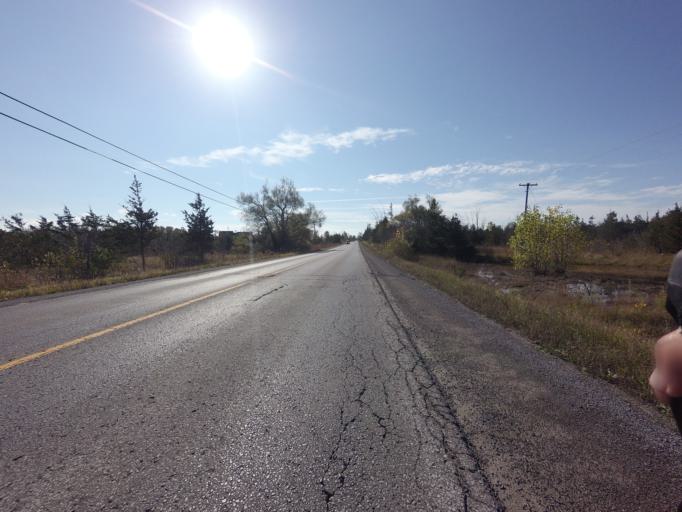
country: CA
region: Ontario
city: Prince Edward
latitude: 44.0190
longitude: -77.3649
